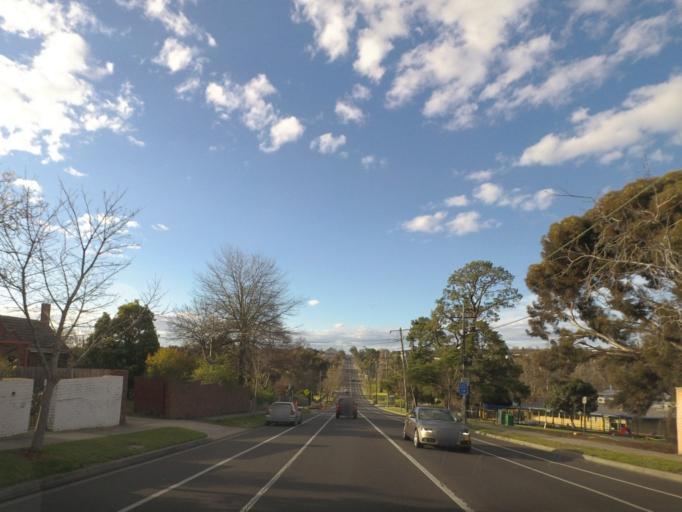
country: AU
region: Victoria
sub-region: Boroondara
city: Balwyn North
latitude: -37.8023
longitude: 145.0834
